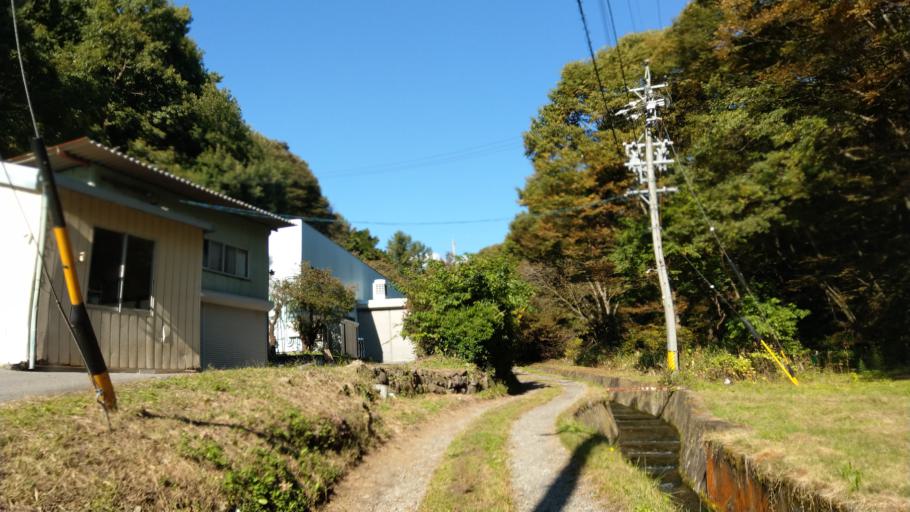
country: JP
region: Nagano
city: Komoro
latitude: 36.3372
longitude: 138.4342
